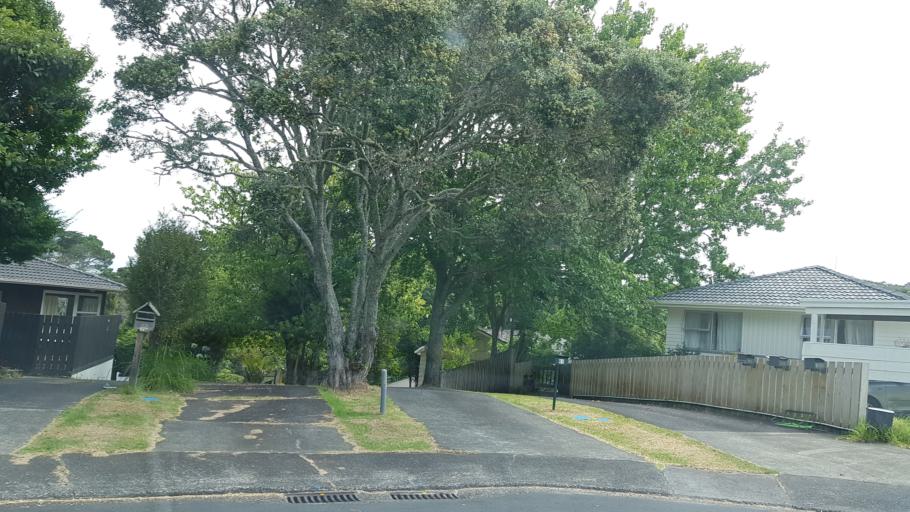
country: NZ
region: Auckland
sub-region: Auckland
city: North Shore
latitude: -36.7781
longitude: 174.7187
